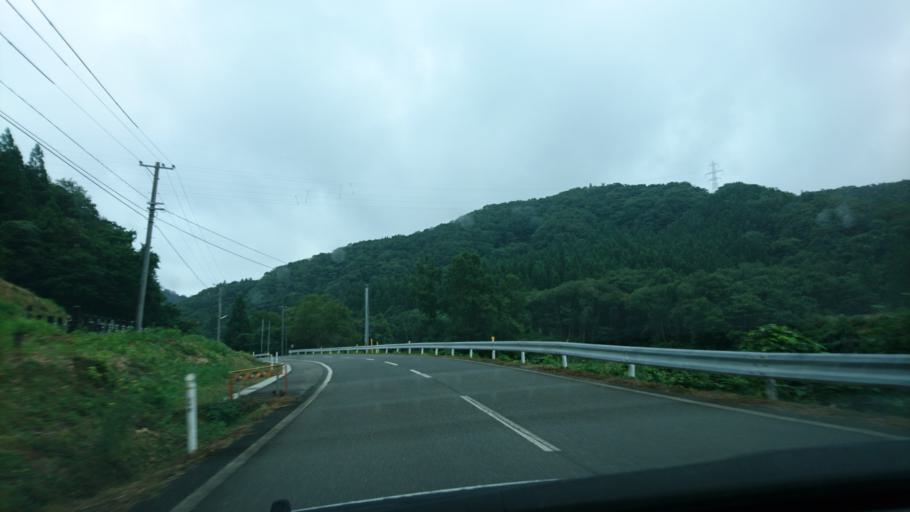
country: JP
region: Iwate
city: Ichinoseki
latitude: 38.8872
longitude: 140.9867
